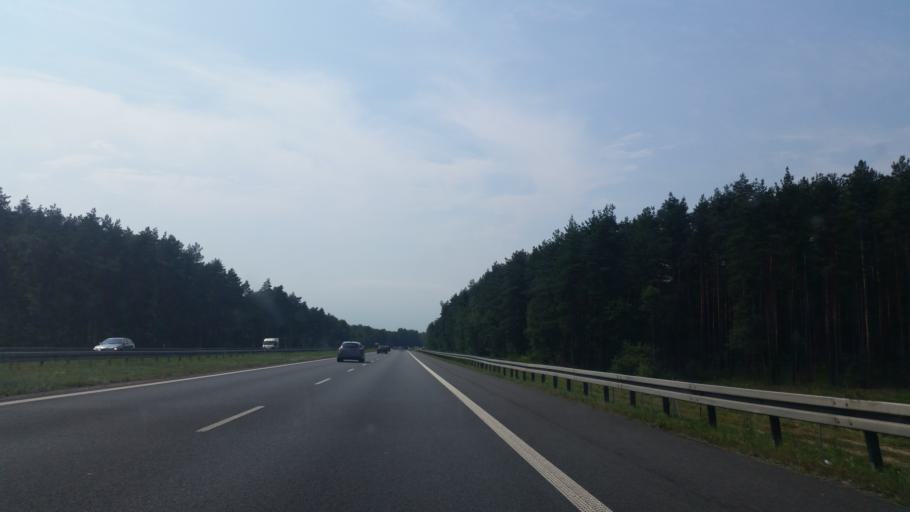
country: PL
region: Lesser Poland Voivodeship
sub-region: Powiat chrzanowski
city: Libiaz
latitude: 50.1499
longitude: 19.3329
